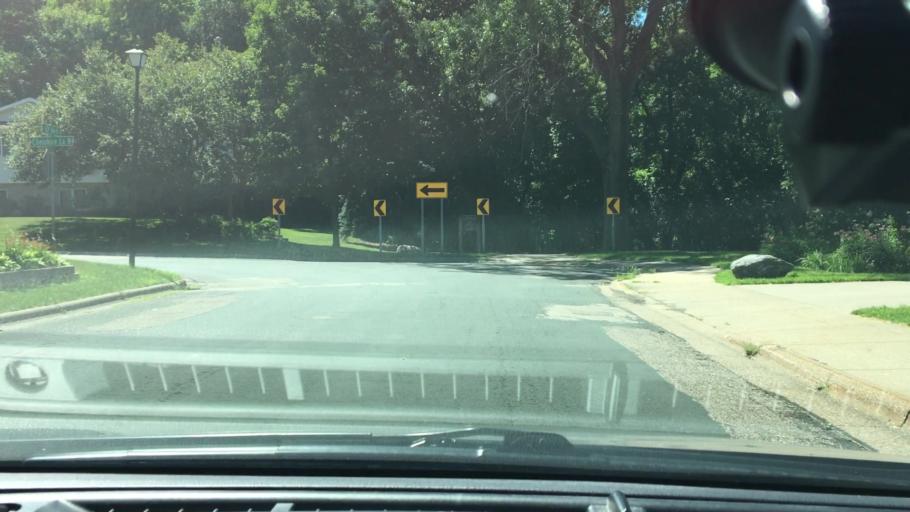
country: US
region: Minnesota
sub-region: Hennepin County
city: Maple Grove
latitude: 45.0694
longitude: -93.4580
